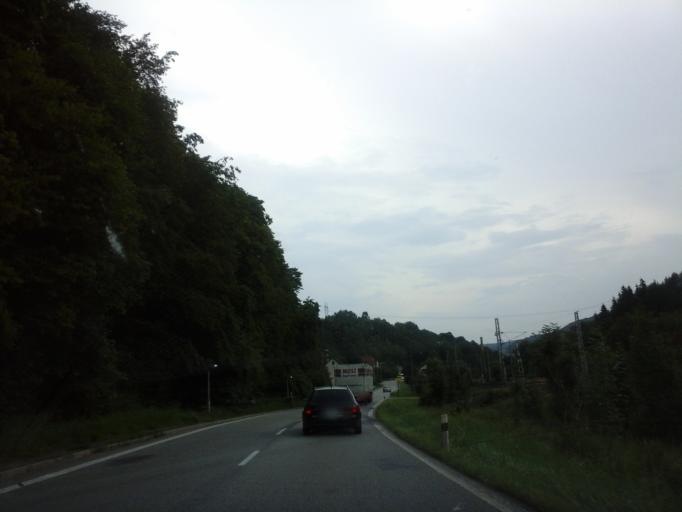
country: CZ
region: Pardubicky
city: Brnenec
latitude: 49.6140
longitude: 16.5316
